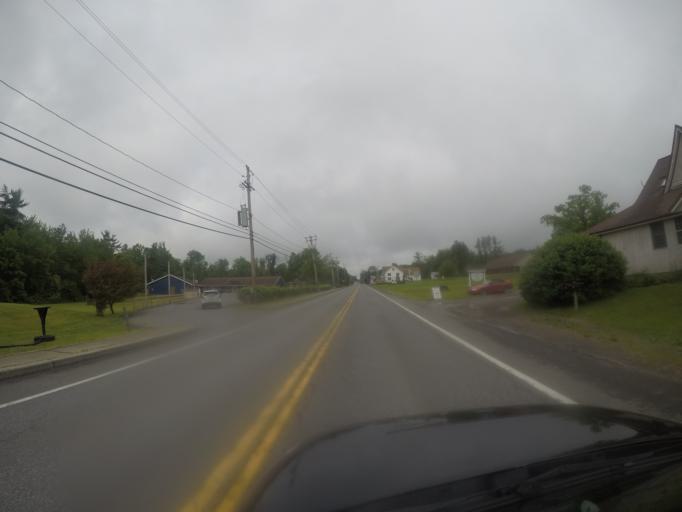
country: US
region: New York
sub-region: Ulster County
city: Shokan
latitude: 41.9742
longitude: -74.2016
